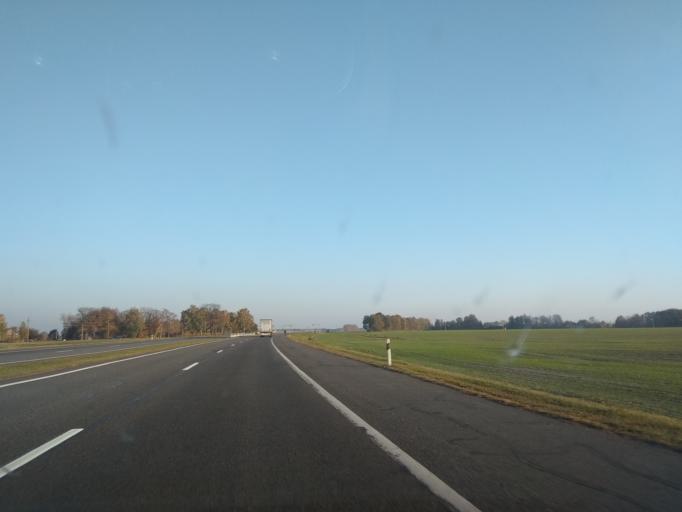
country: BY
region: Brest
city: Kobryn
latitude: 52.1975
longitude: 24.2985
